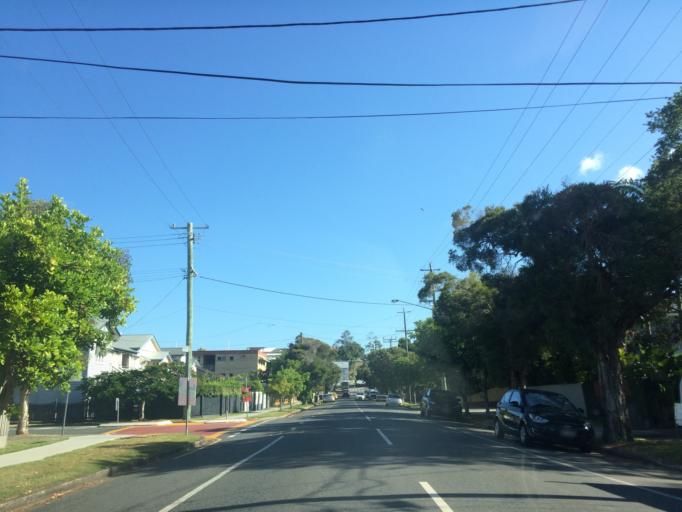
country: AU
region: Queensland
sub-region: Brisbane
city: Balmoral
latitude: -27.4542
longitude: 153.0618
